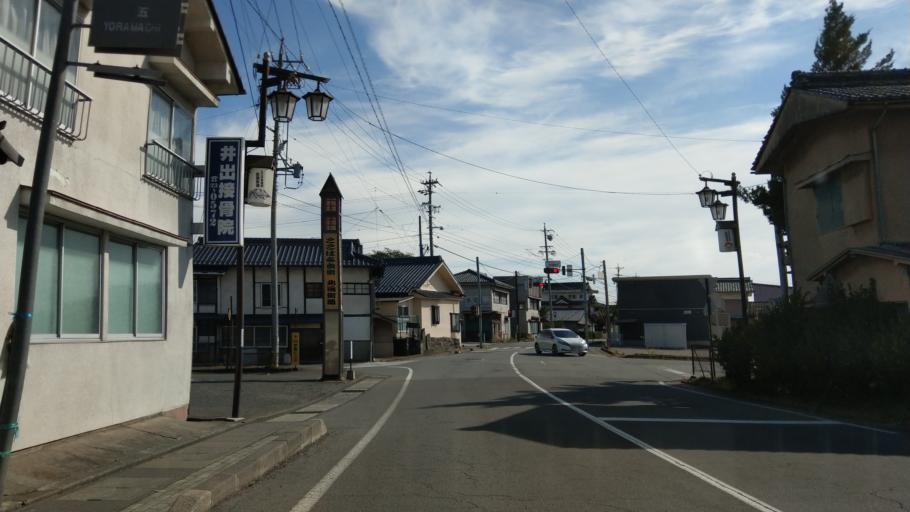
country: JP
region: Nagano
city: Komoro
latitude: 36.3221
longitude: 138.4325
